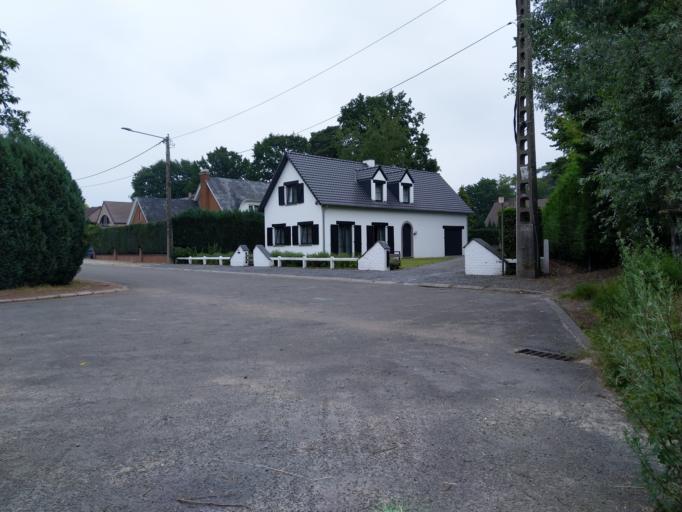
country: BE
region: Wallonia
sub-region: Province du Hainaut
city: Mons
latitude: 50.4885
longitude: 3.9360
